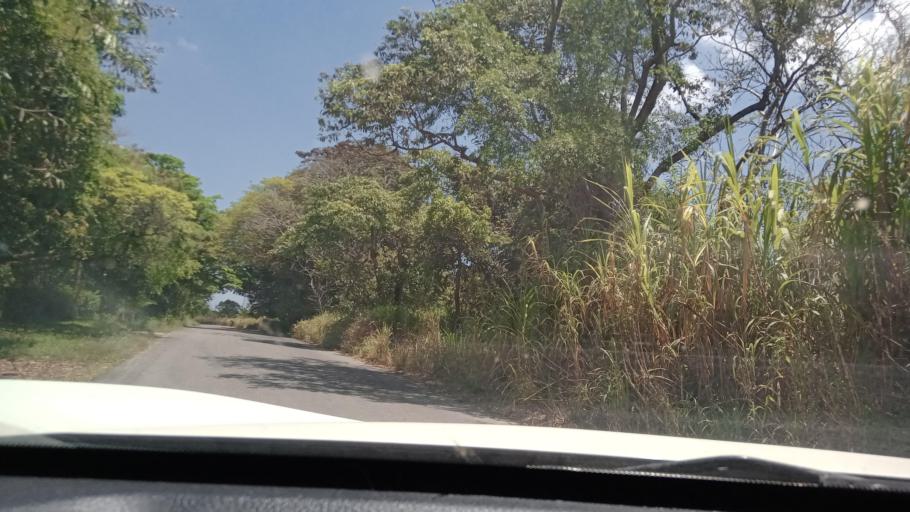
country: MX
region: Veracruz
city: Las Choapas
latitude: 17.7691
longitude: -94.1078
